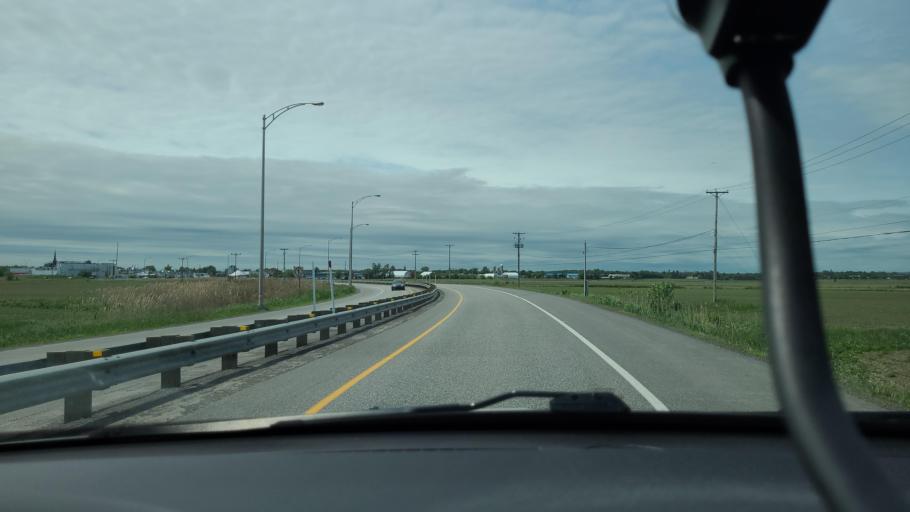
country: CA
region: Quebec
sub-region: Lanaudiere
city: Sainte-Julienne
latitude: 45.9127
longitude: -73.6543
